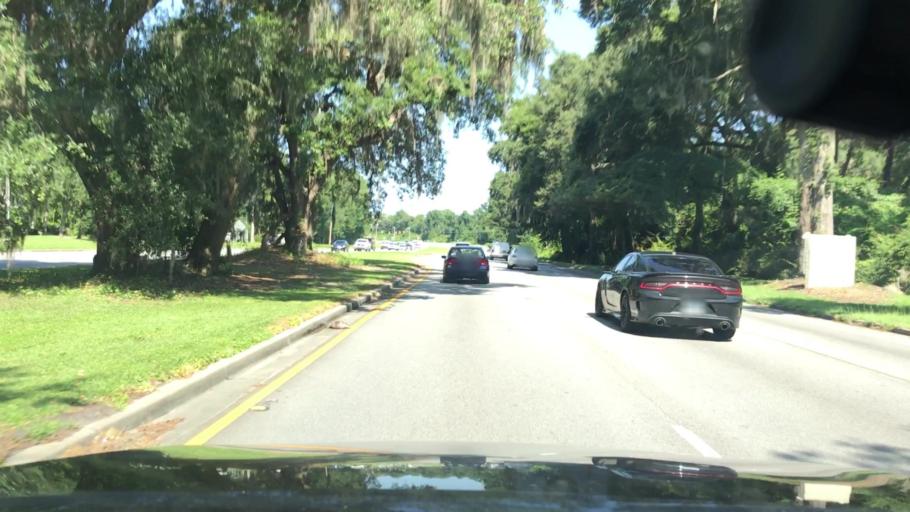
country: US
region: South Carolina
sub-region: Beaufort County
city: Bluffton
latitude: 32.2389
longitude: -80.8121
